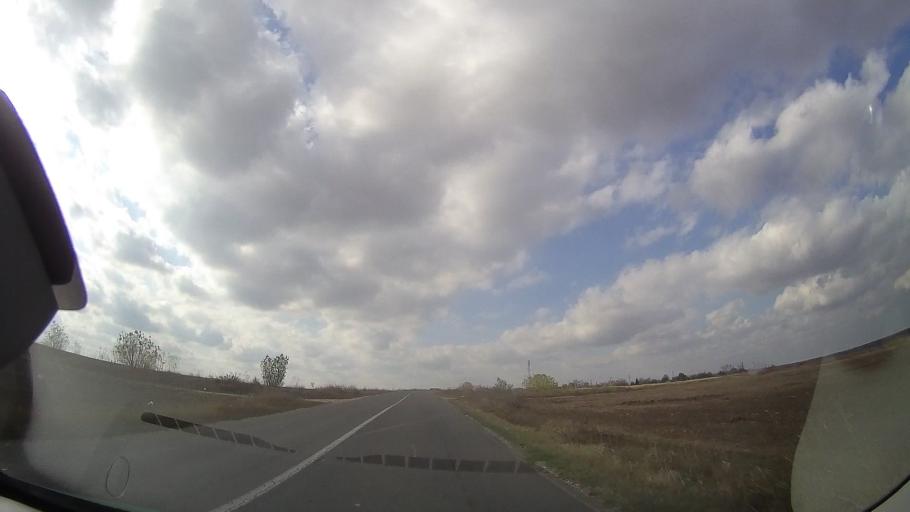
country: RO
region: Constanta
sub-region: Comuna Pecineaga
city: Pecineaga
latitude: 43.8975
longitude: 28.5183
